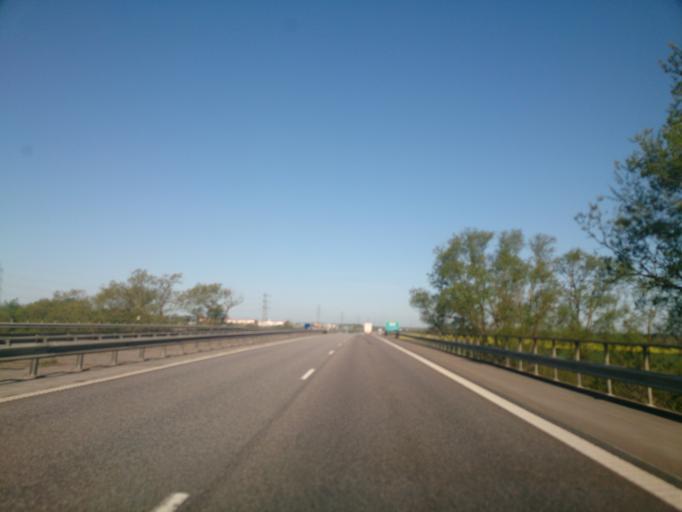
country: SE
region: OEstergoetland
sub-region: Linkopings Kommun
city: Linkoping
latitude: 58.4336
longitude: 15.6241
